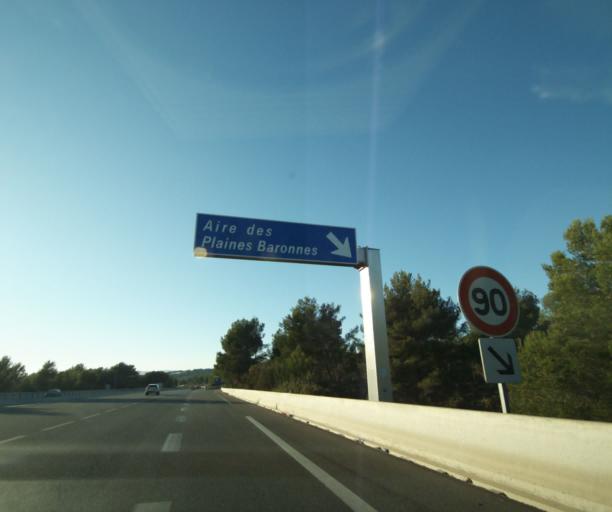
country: FR
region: Provence-Alpes-Cote d'Azur
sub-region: Departement du Var
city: Saint-Cyr-sur-Mer
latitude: 43.1929
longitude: 5.6753
